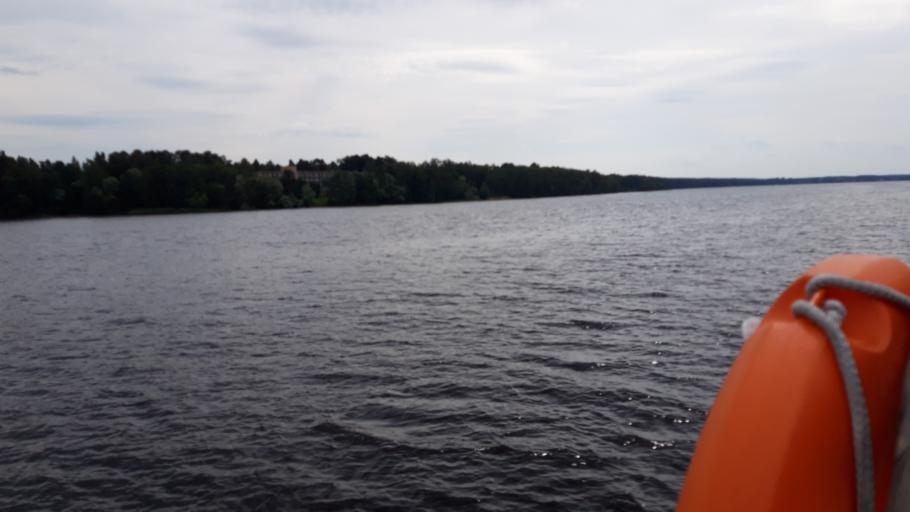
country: RU
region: Tverskaya
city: Konakovo
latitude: 56.6940
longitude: 36.6982
